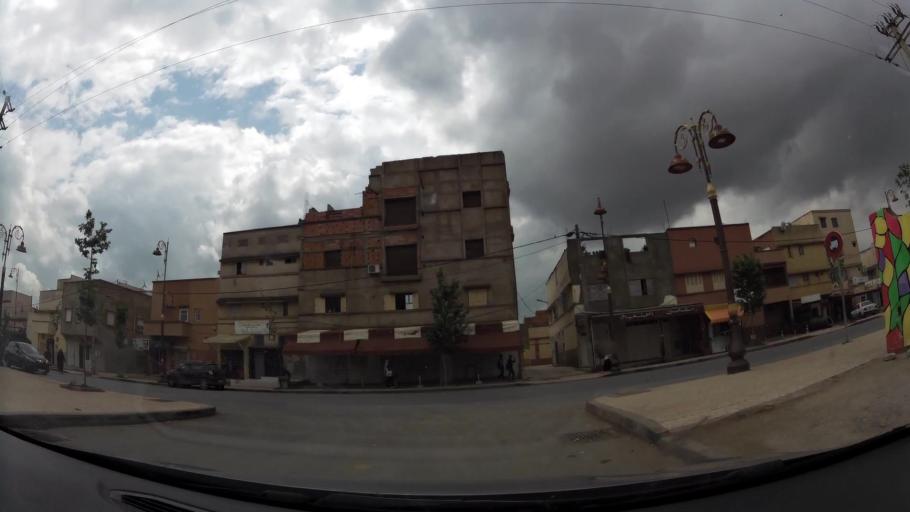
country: MA
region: Rabat-Sale-Zemmour-Zaer
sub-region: Khemisset
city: Tiflet
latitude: 33.8887
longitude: -6.3152
